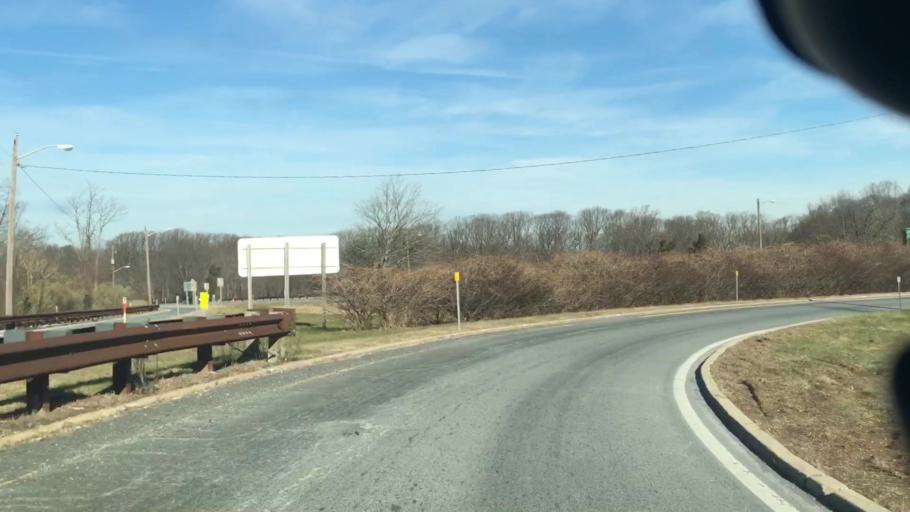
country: US
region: New Jersey
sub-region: Monmouth County
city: Lincroft
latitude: 40.3763
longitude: -74.1515
